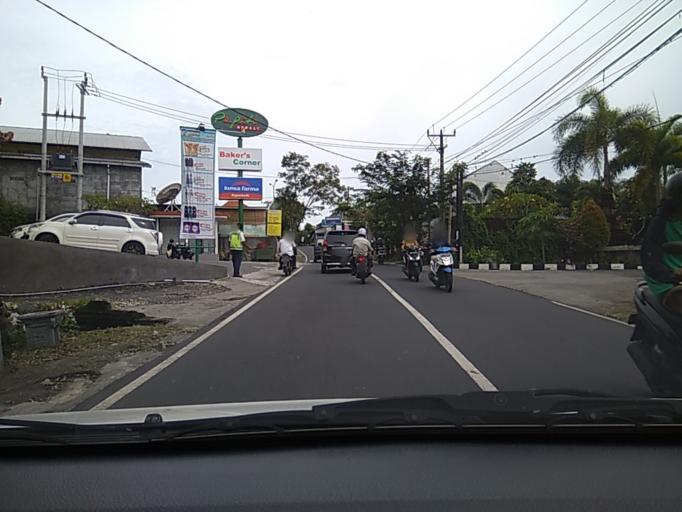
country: ID
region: Bali
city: Banjar Kerobokan
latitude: -8.6307
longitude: 115.1329
